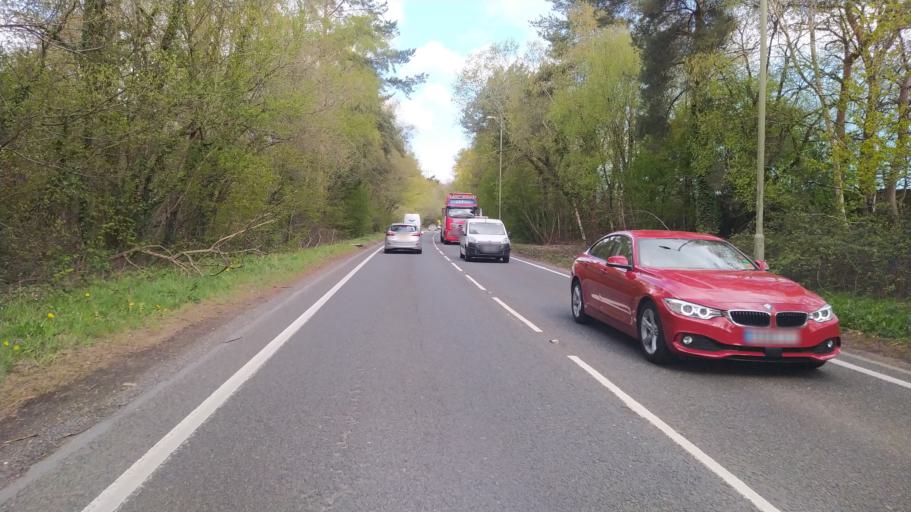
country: GB
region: England
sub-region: Hampshire
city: Marchwood
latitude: 50.8873
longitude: -1.4623
